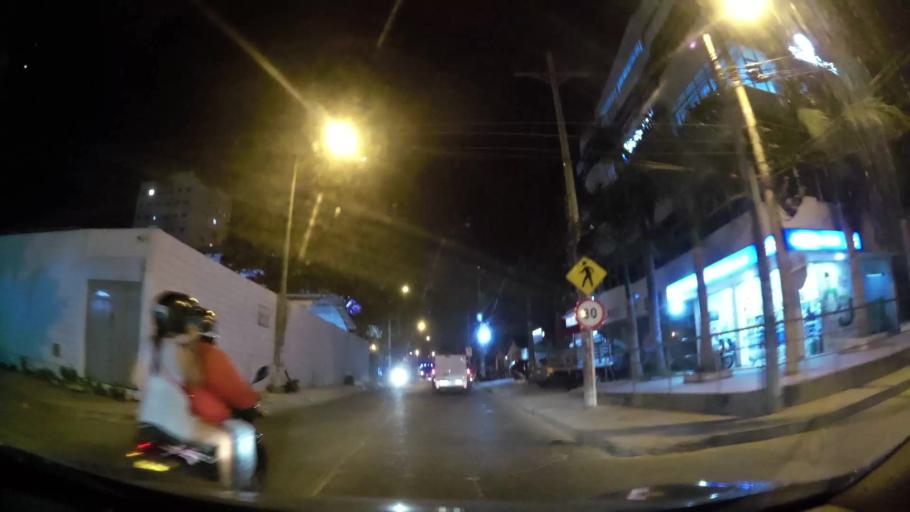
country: CO
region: Bolivar
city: Cartagena
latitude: 10.4062
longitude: -75.5113
